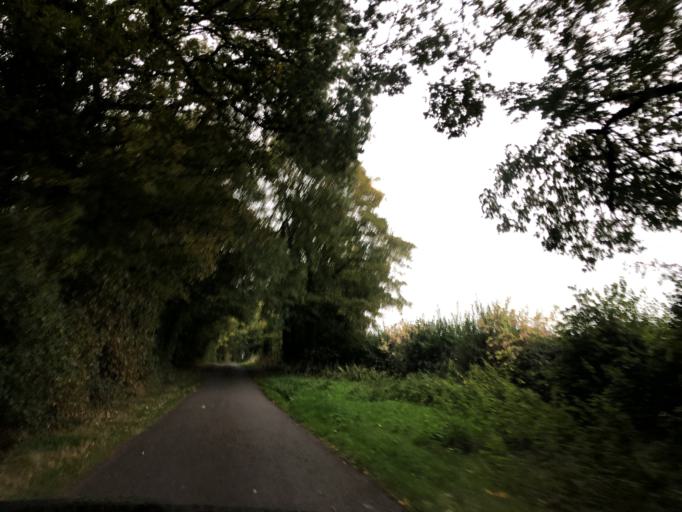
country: GB
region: England
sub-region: Warwickshire
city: Wroxall
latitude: 52.3282
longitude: -1.6523
